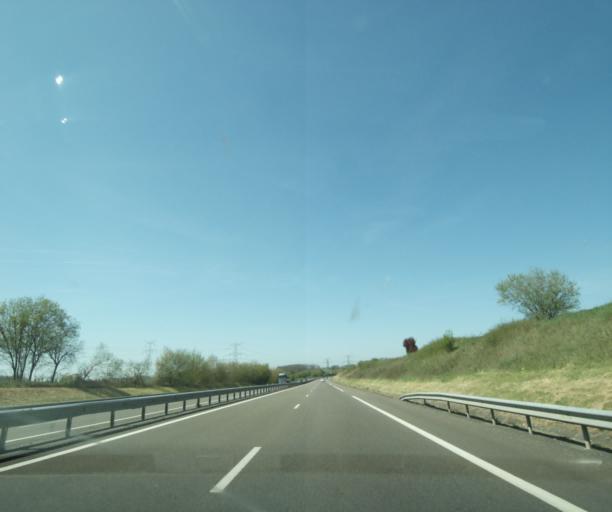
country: FR
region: Bourgogne
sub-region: Departement de la Nievre
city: Coulanges-les-Nevers
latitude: 47.0250
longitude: 3.1786
